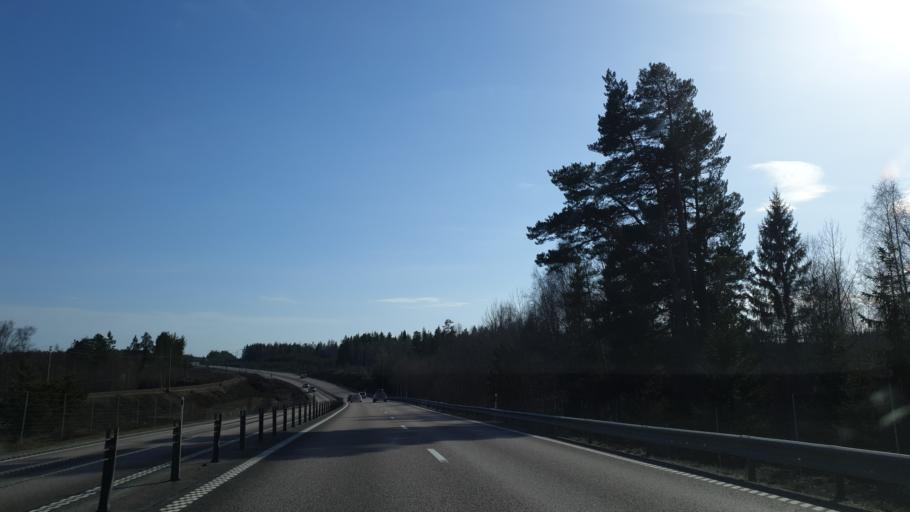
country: SE
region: Gaevleborg
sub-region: Hudiksvalls Kommun
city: Hudiksvall
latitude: 61.8355
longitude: 17.1933
